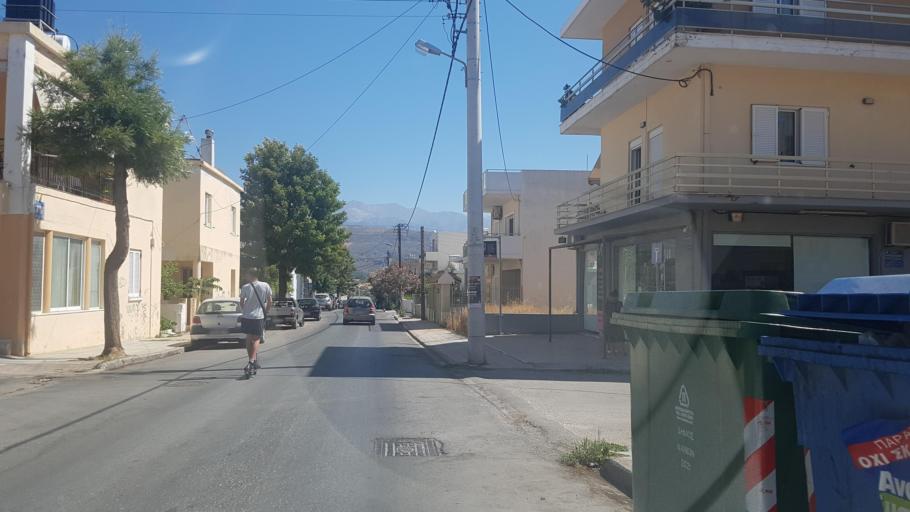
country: GR
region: Crete
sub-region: Nomos Chanias
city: Chania
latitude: 35.5065
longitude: 24.0177
